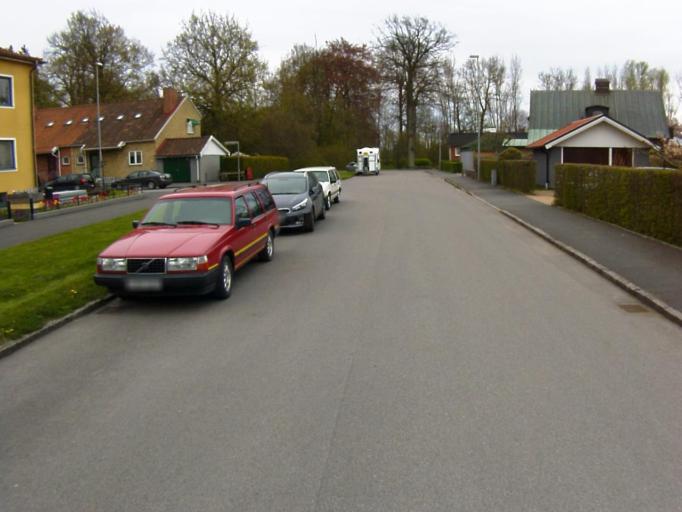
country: SE
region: Skane
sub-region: Kristianstads Kommun
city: Kristianstad
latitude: 56.0197
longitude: 14.1622
